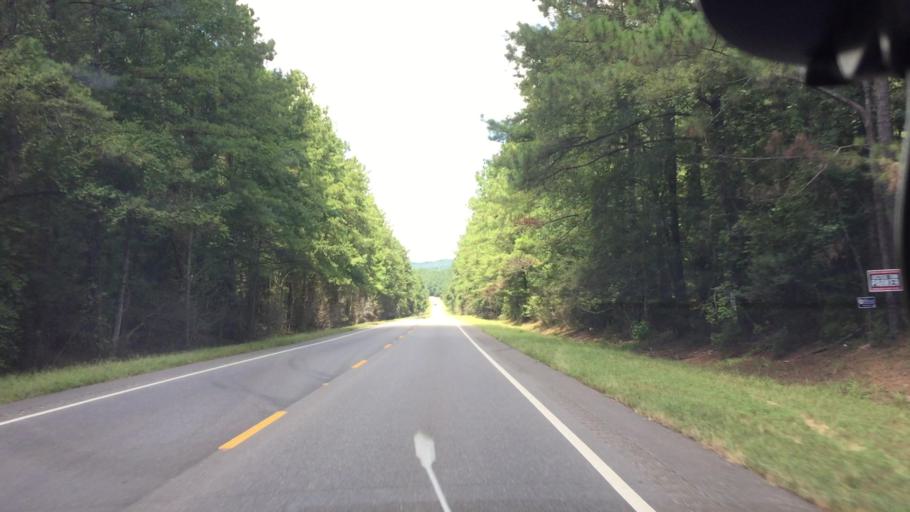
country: US
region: Alabama
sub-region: Coffee County
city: New Brockton
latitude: 31.4551
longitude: -85.8968
